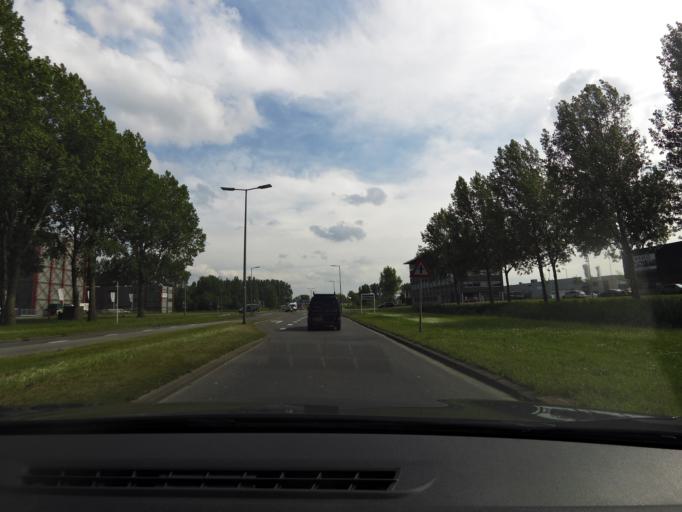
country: NL
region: South Holland
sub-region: Gemeente Schiedam
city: Schiedam
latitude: 51.9406
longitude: 4.4103
